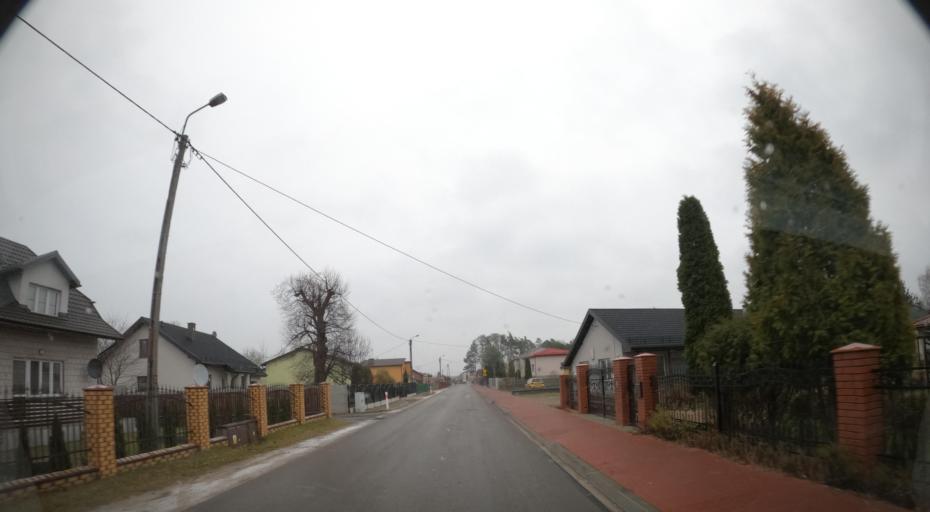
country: PL
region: Masovian Voivodeship
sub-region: Powiat radomski
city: Jedlnia-Letnisko
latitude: 51.4171
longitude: 21.2808
